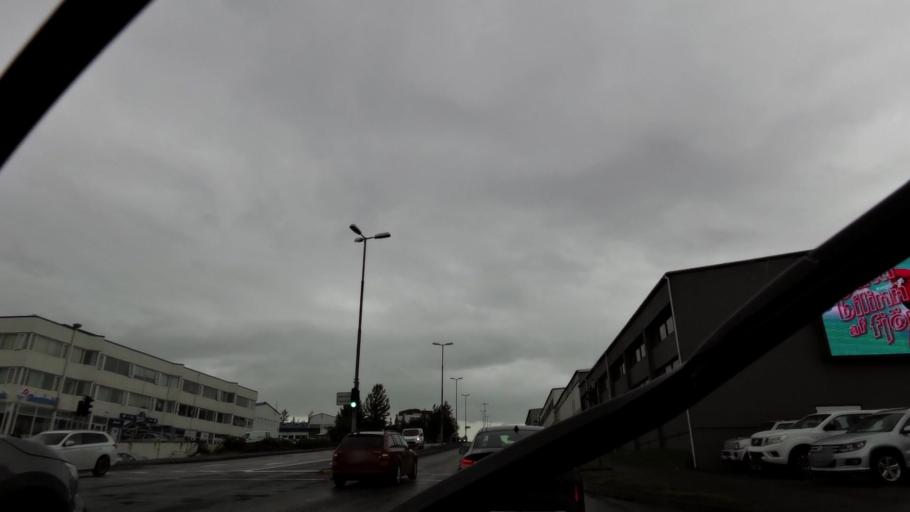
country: IS
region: Capital Region
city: Reykjavik
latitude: 64.1286
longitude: -21.8125
